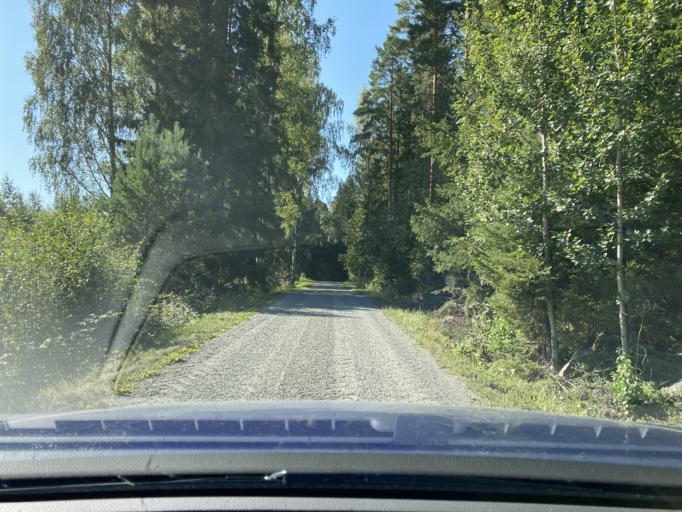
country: FI
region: Satakunta
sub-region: Rauma
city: Kiukainen
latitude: 61.1461
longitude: 22.0144
